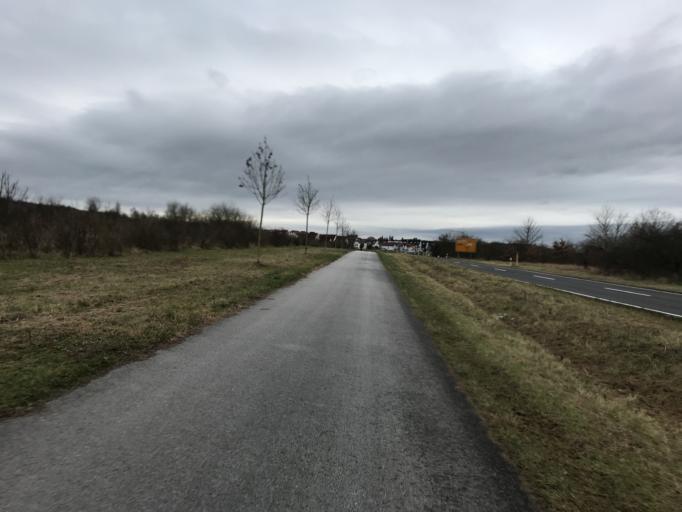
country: DE
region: Rheinland-Pfalz
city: Nieder-Ingelheim
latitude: 49.9886
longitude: 8.0768
